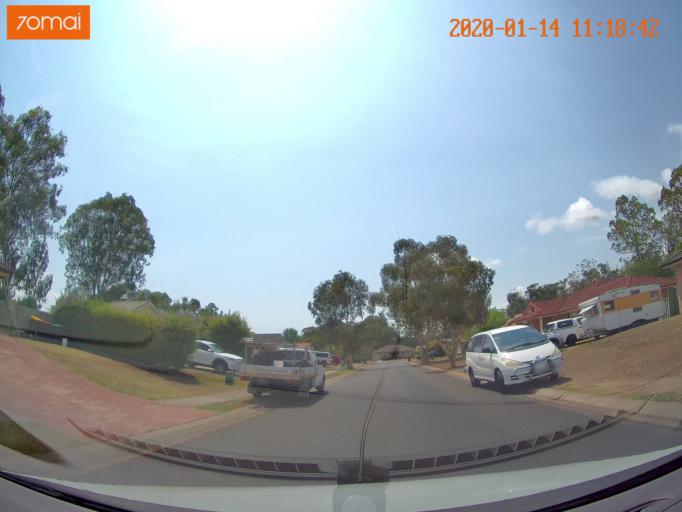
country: AU
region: New South Wales
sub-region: Lake Macquarie Shire
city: Cooranbong
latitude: -33.0976
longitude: 151.4612
